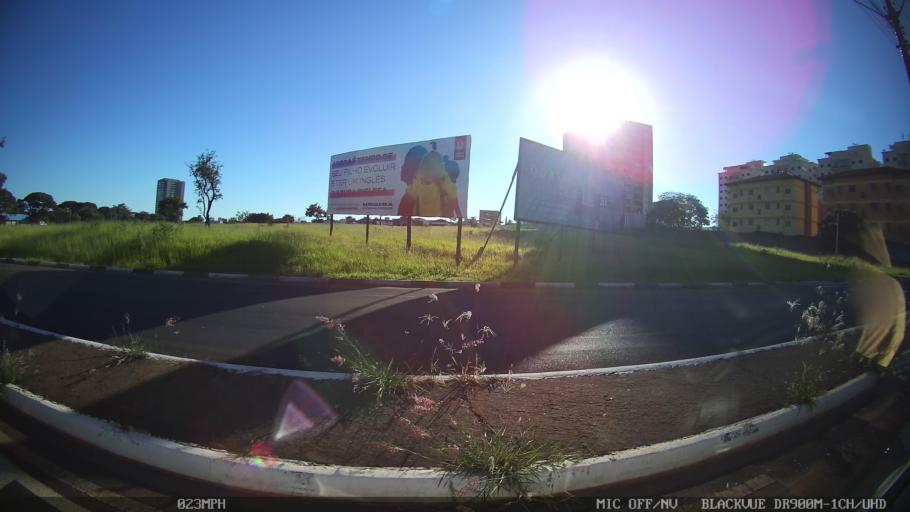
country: BR
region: Sao Paulo
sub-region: Franca
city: Franca
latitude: -20.5641
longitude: -47.4060
